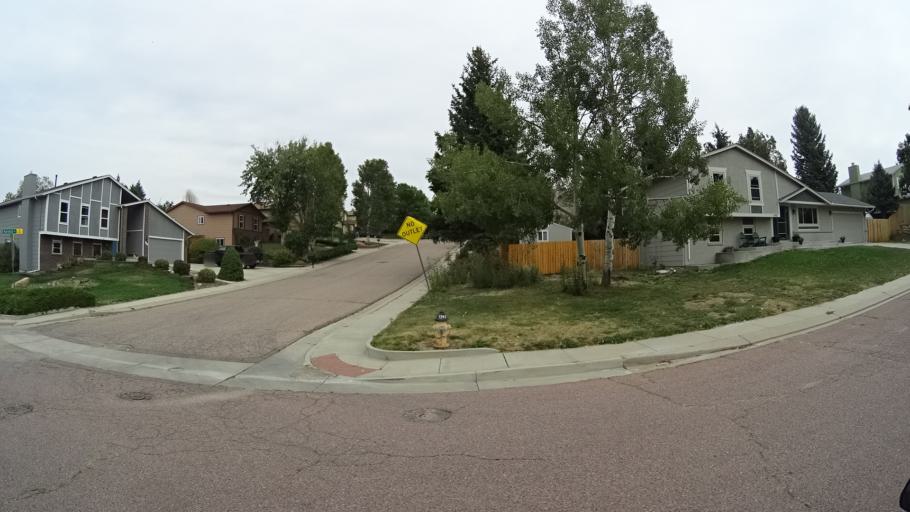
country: US
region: Colorado
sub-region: El Paso County
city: Cimarron Hills
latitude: 38.9051
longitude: -104.7323
